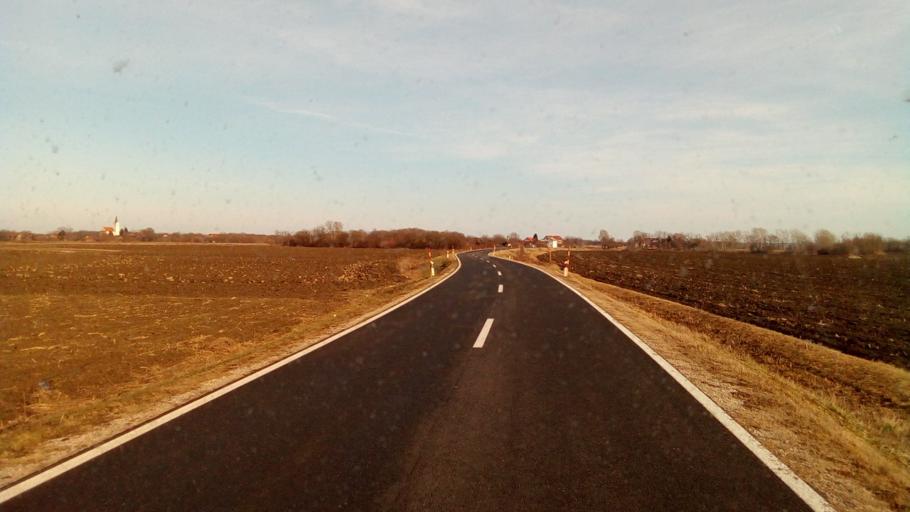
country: HR
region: Medimurska
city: Kotoriba
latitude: 46.3212
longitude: 16.7707
